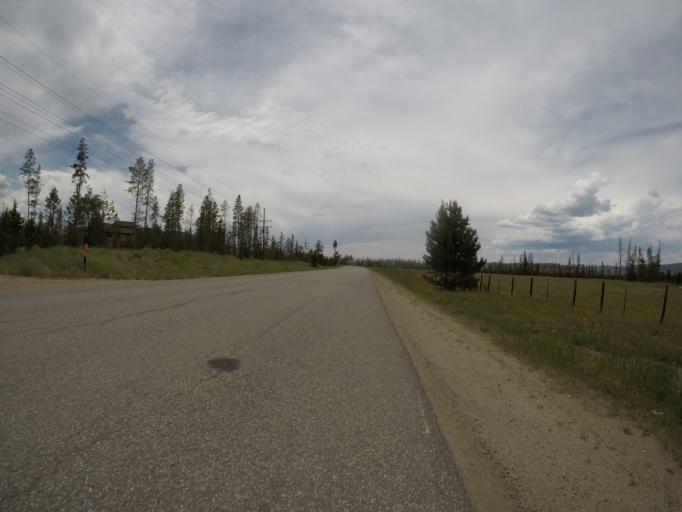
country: US
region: Colorado
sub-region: Grand County
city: Fraser
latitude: 39.9559
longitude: -105.8426
